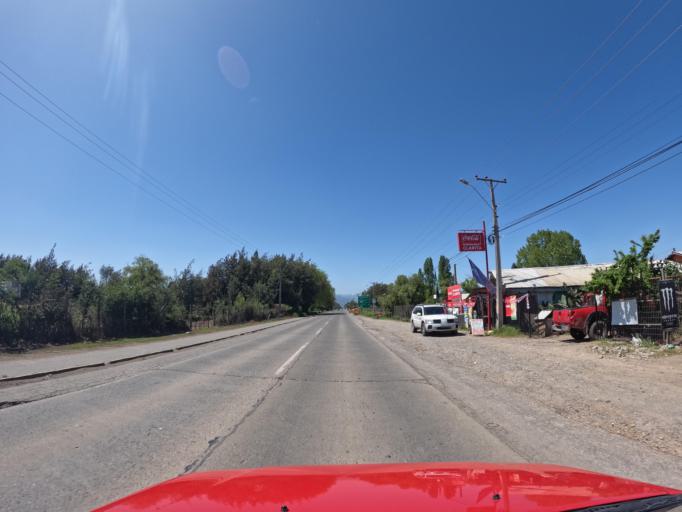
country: CL
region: Maule
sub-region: Provincia de Linares
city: Linares
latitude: -35.8330
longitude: -71.5339
